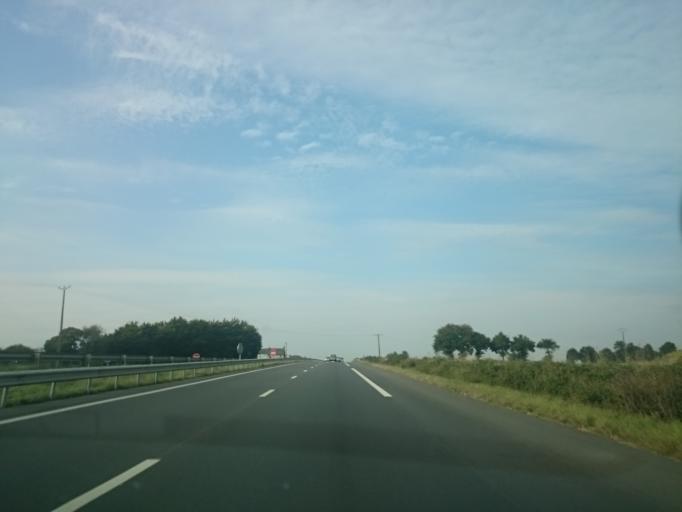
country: FR
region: Brittany
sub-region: Departement d'Ille-et-Vilaine
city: Quedillac
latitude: 48.2274
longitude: -2.1161
